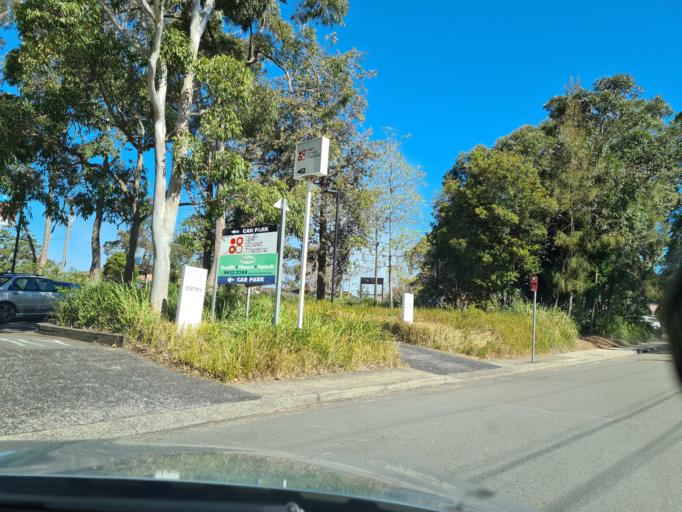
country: AU
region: New South Wales
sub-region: Warringah
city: Davidson
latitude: -33.7402
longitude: 151.2095
